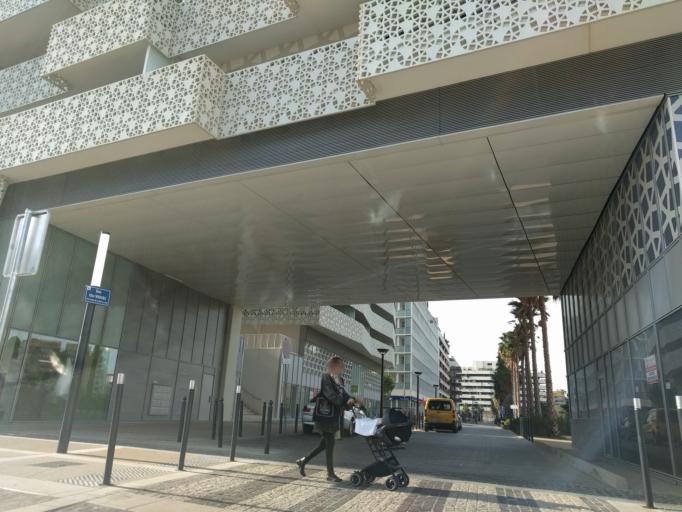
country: FR
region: Languedoc-Roussillon
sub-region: Departement de l'Herault
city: Montpellier
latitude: 43.5997
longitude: 3.9020
